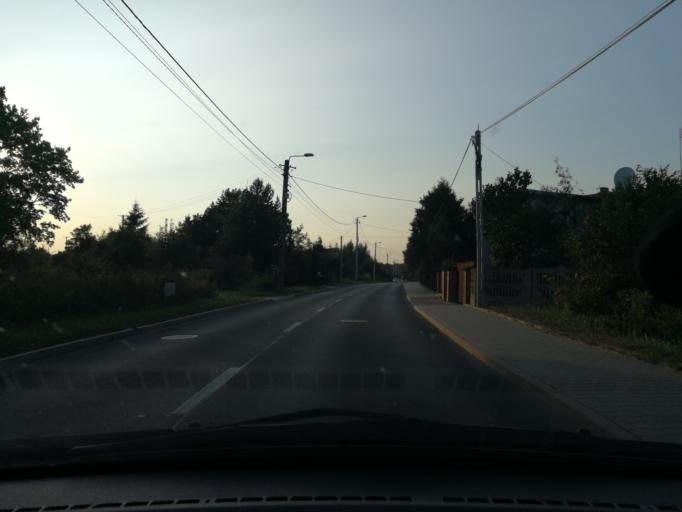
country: PL
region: Lodz Voivodeship
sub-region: Skierniewice
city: Skierniewice
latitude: 51.9707
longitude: 20.1312
